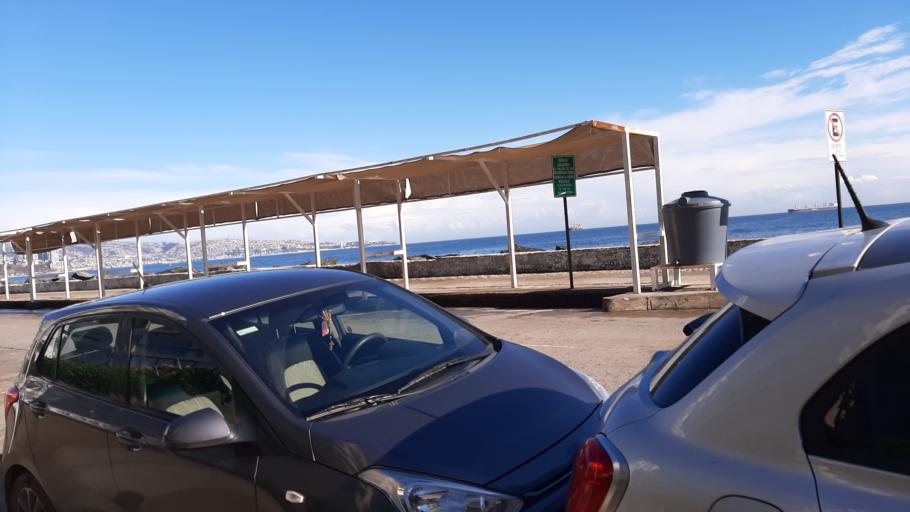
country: CL
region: Valparaiso
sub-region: Provincia de Valparaiso
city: Vina del Mar
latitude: -33.0146
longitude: -71.5567
